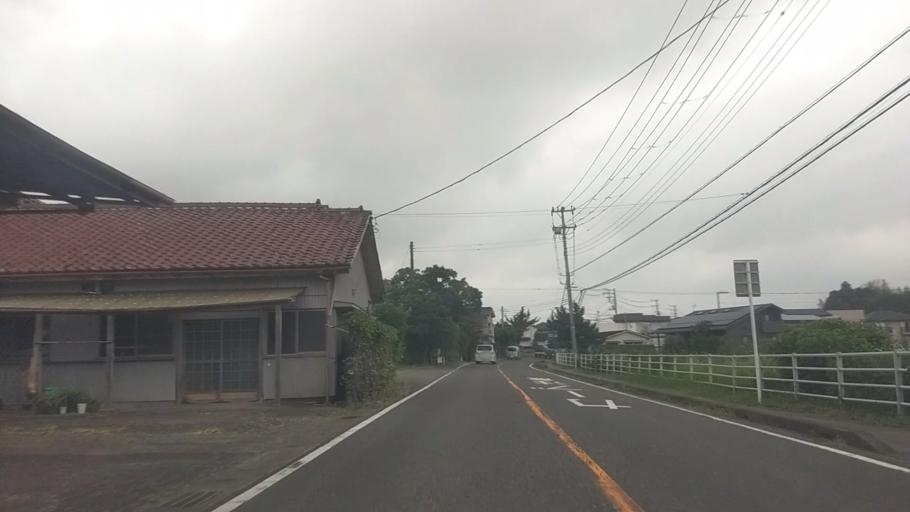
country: JP
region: Chiba
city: Kawaguchi
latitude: 35.1092
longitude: 140.0846
